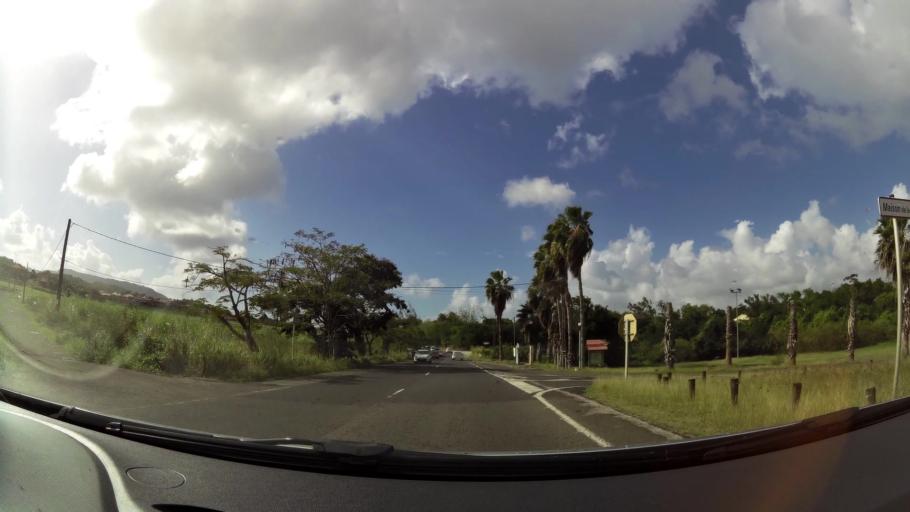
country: MQ
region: Martinique
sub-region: Martinique
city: Les Trois-Ilets
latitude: 14.5331
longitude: -61.0243
